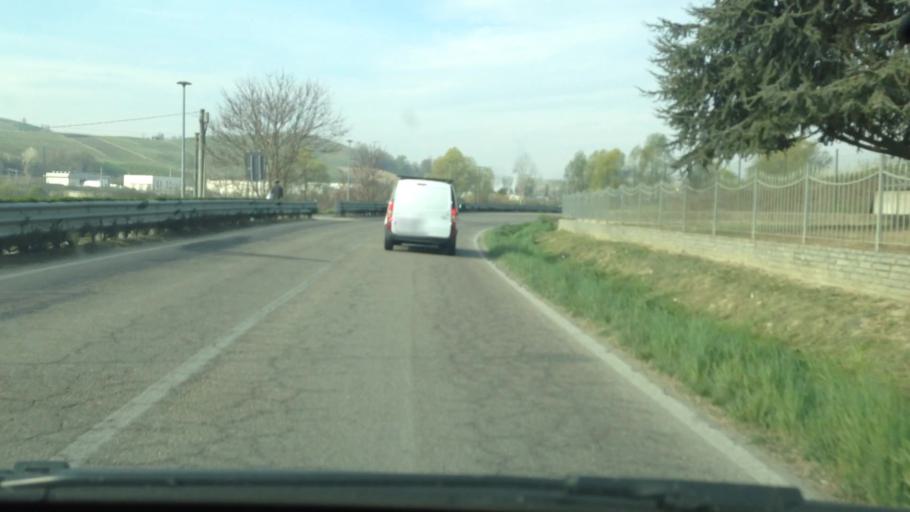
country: IT
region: Piedmont
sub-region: Provincia di Cuneo
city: Canale
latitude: 44.8008
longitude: 8.0159
